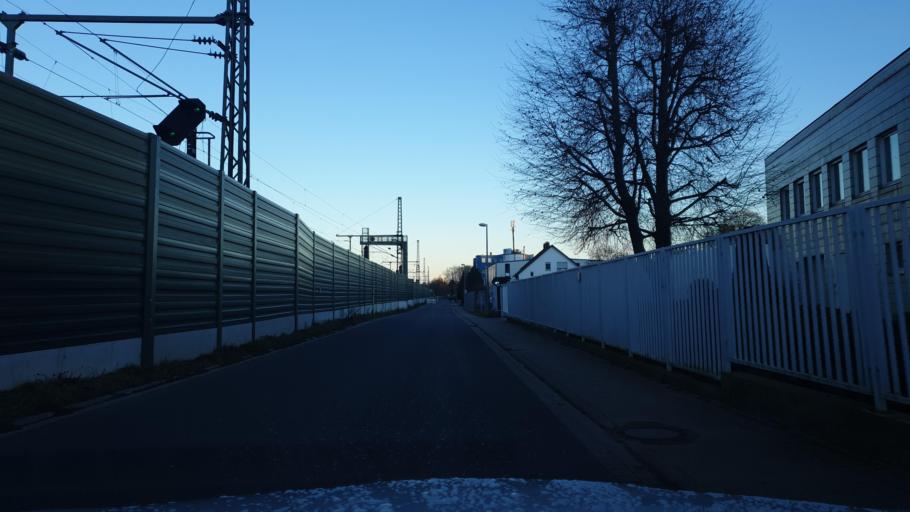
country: DE
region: North Rhine-Westphalia
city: Bad Oeynhausen
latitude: 52.2081
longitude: 8.8318
